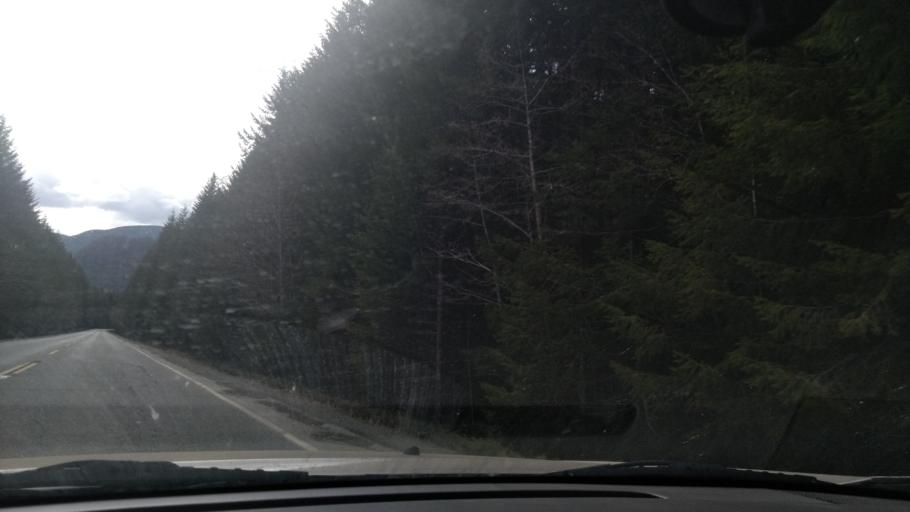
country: CA
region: British Columbia
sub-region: Regional District of Alberni-Clayoquot
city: Tofino
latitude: 49.8345
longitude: -125.9593
